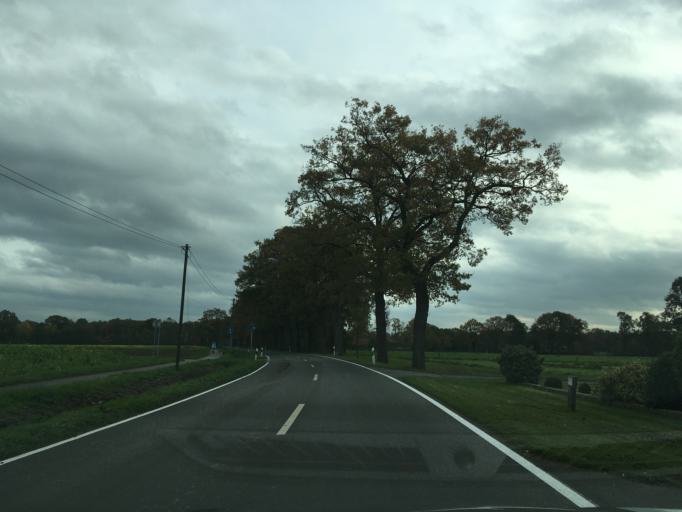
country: DE
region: North Rhine-Westphalia
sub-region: Regierungsbezirk Munster
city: Vreden
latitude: 52.0868
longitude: 6.8927
